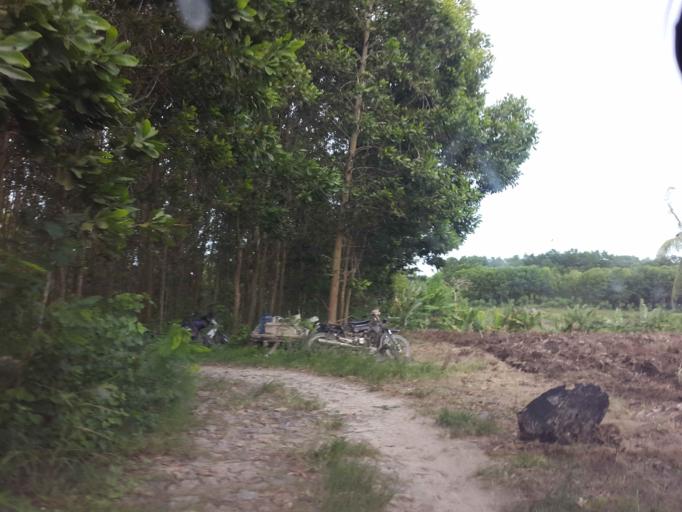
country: ID
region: Lampung
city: Palas
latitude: -5.5978
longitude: 105.6155
